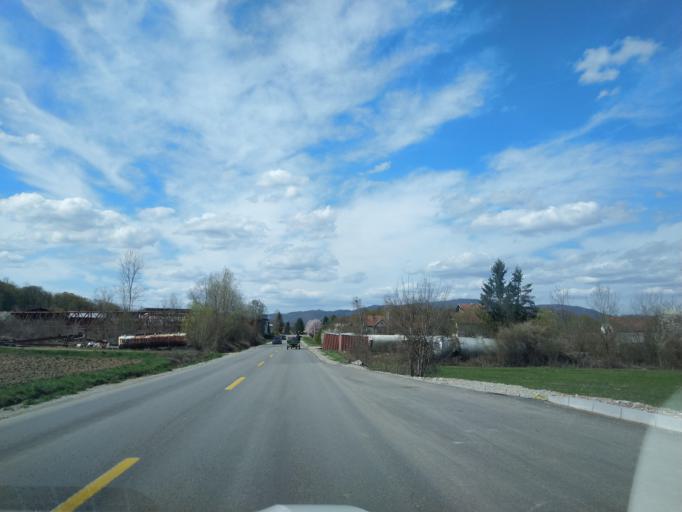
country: RS
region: Central Serbia
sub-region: Zlatiborski Okrug
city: Pozega
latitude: 43.8154
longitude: 20.0879
